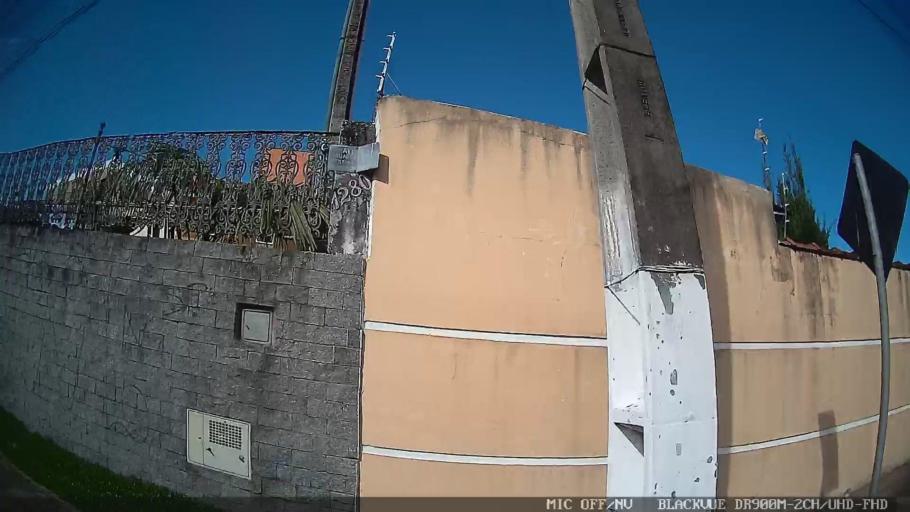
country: BR
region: Sao Paulo
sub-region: Iguape
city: Iguape
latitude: -24.7033
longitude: -47.5644
